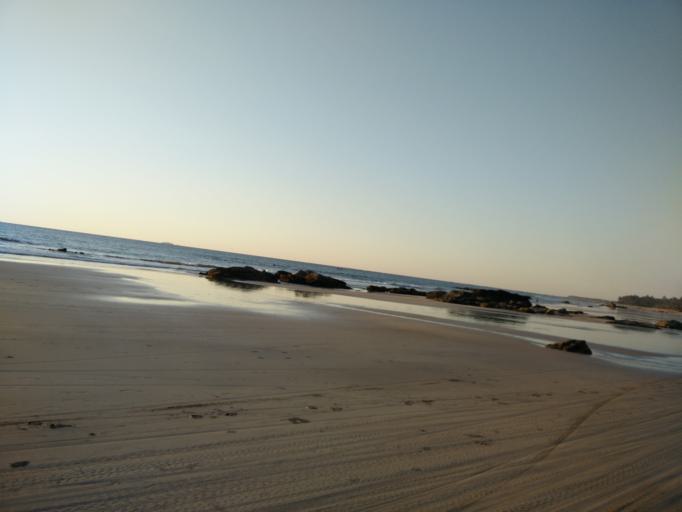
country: MM
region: Ayeyarwady
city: Pathein
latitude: 16.8230
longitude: 94.3968
